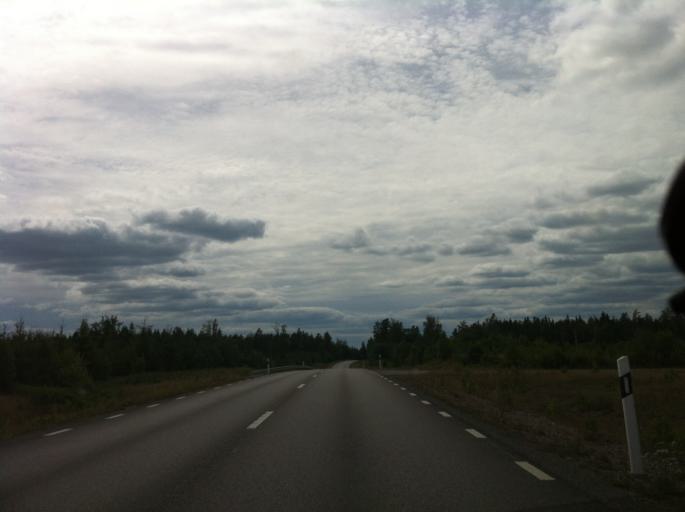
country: SE
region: Kronoberg
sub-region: Tingsryds Kommun
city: Tingsryd
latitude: 56.5022
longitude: 15.0922
